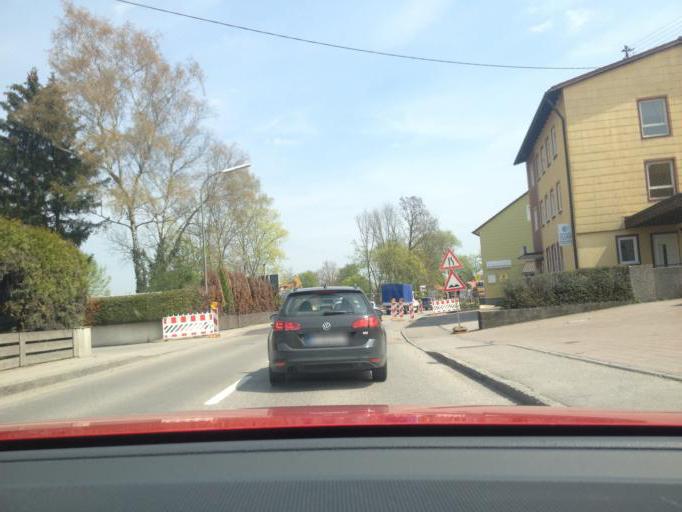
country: DE
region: Bavaria
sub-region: Upper Bavaria
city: Allershausen
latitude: 48.4306
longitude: 11.5960
